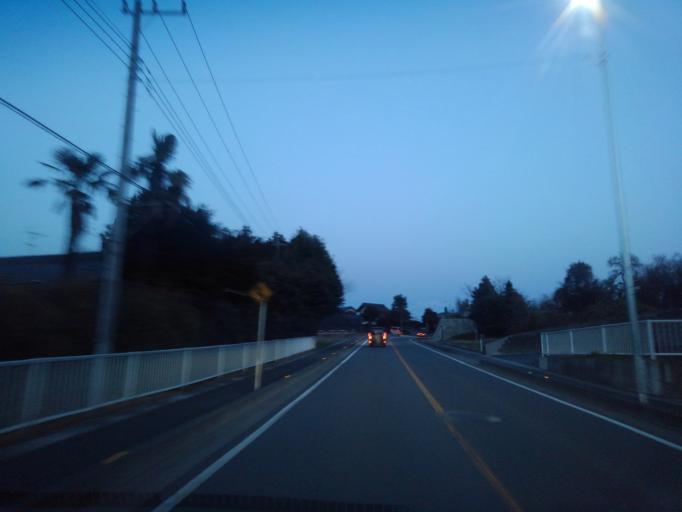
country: JP
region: Saitama
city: Hanno
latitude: 35.8830
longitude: 139.3031
